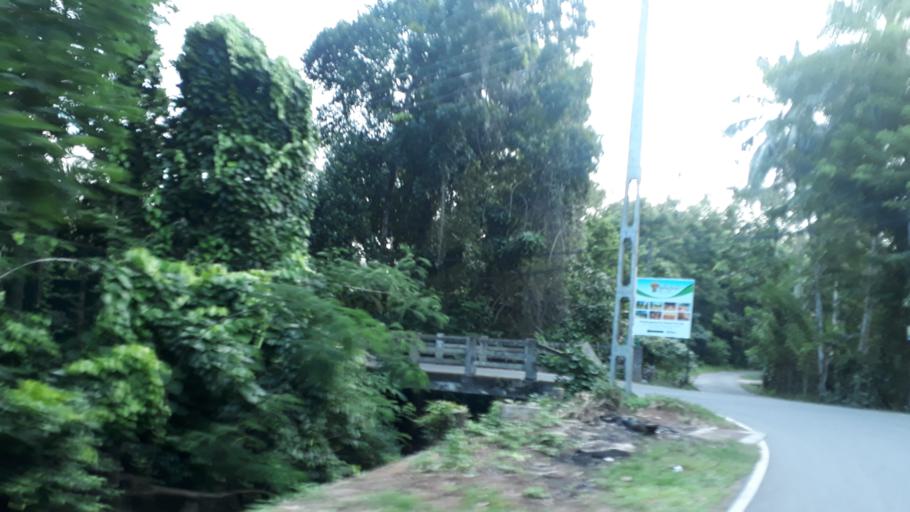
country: LK
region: Western
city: Gampaha
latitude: 7.1027
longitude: 79.9859
